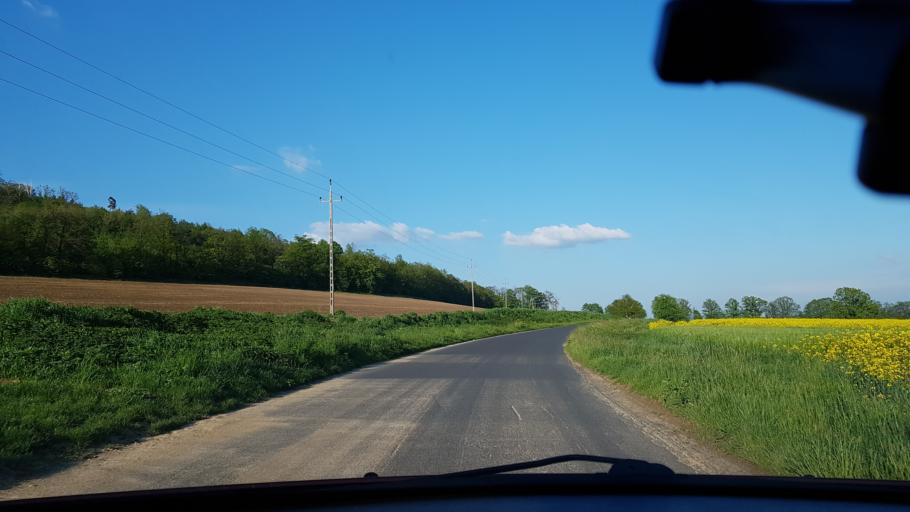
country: PL
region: Lower Silesian Voivodeship
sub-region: Powiat zabkowicki
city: Budzow
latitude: 50.6130
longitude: 16.6825
